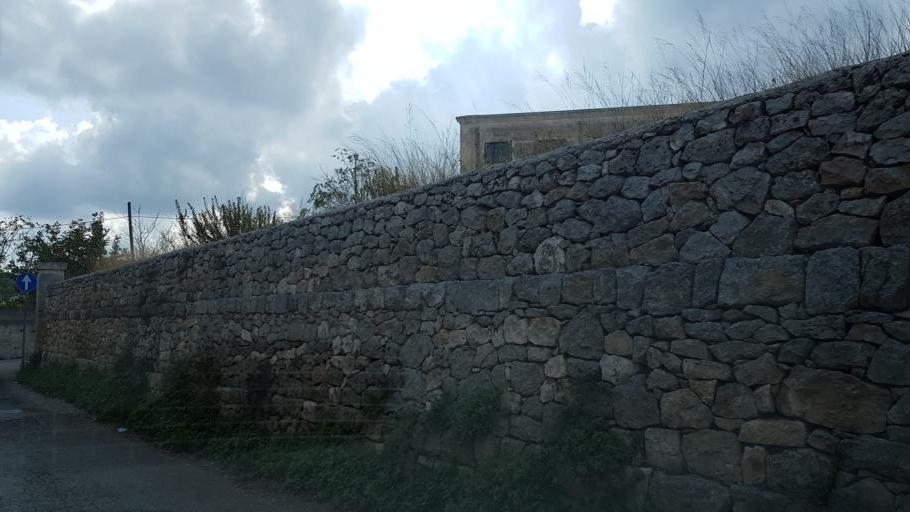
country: IT
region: Apulia
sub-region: Provincia di Brindisi
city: Ostuni
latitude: 40.7342
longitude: 17.5813
